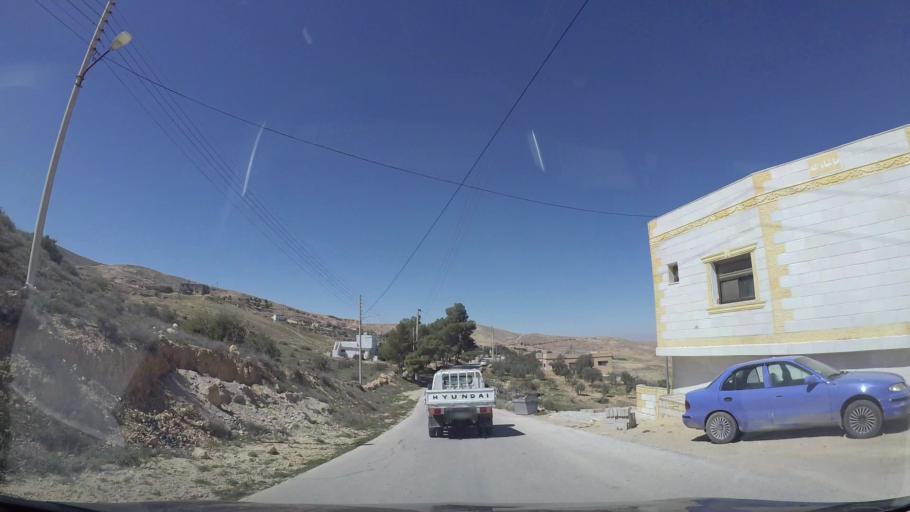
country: JO
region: Tafielah
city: At Tafilah
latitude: 30.8389
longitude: 35.5735
